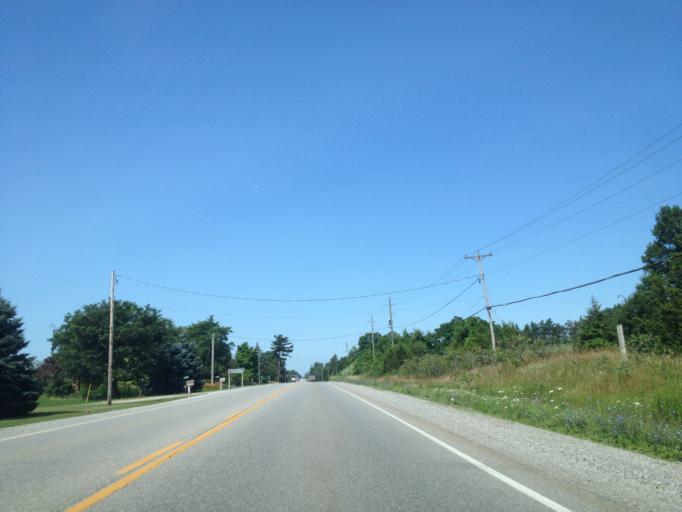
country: CA
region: Ontario
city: Norfolk County
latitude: 42.8366
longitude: -80.3584
